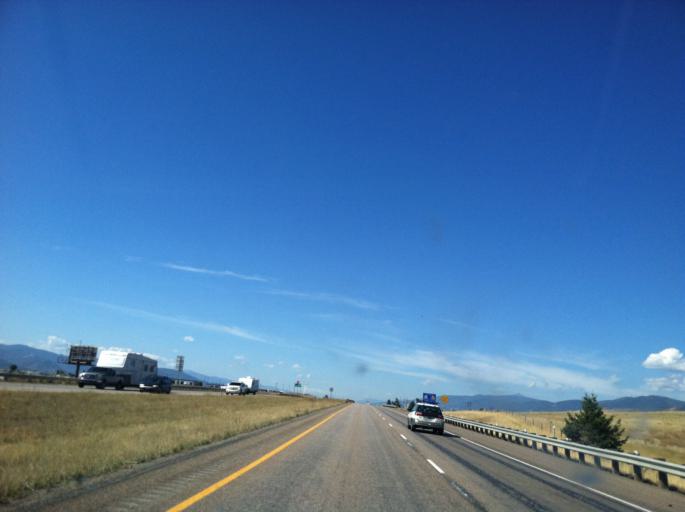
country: US
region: Montana
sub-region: Missoula County
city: Orchard Homes
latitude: 46.9436
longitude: -114.1176
